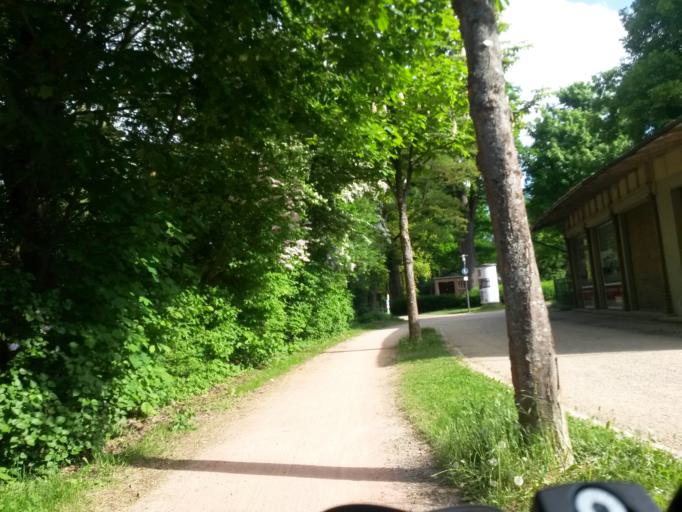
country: DE
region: Bavaria
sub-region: Regierungsbezirk Unterfranken
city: Bad Kissingen
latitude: 50.2081
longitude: 10.0723
